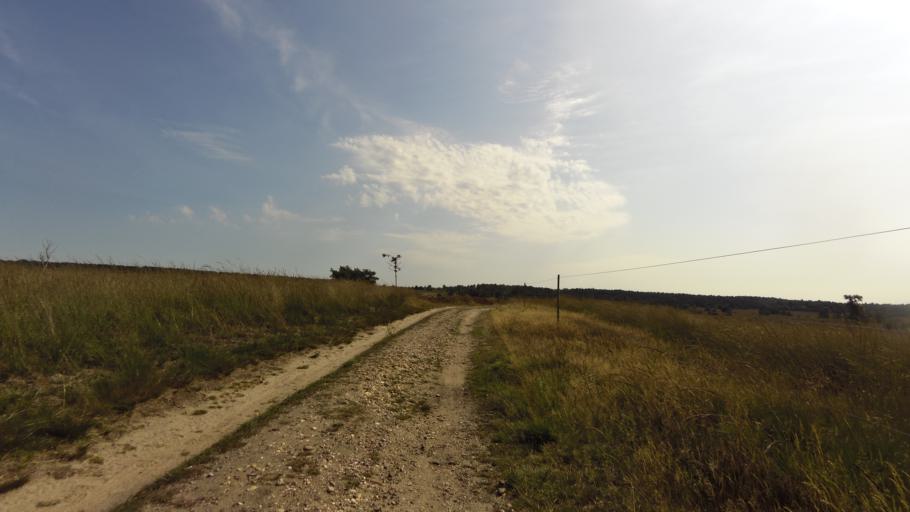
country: NL
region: Gelderland
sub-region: Gemeente Ede
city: Otterlo
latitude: 52.1647
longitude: 5.8442
